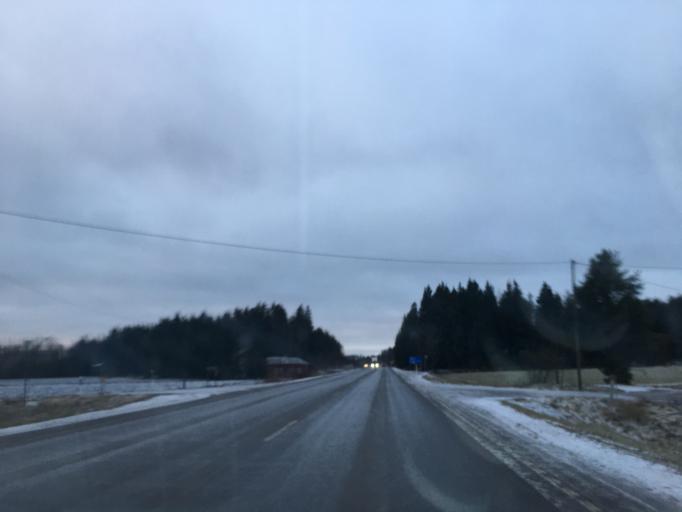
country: FI
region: Varsinais-Suomi
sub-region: Loimaa
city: Aura
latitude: 60.6546
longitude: 22.5552
